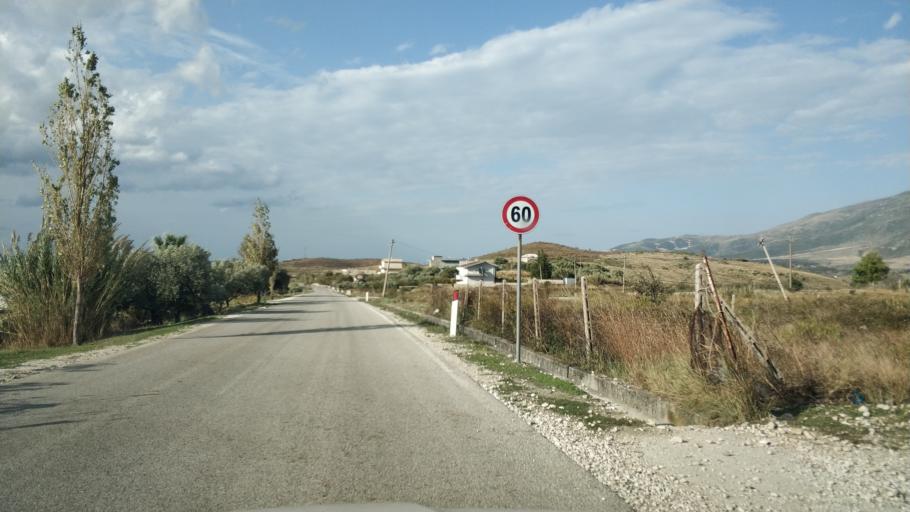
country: AL
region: Vlore
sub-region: Rrethi i Vlores
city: Orikum
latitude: 40.3065
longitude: 19.4820
